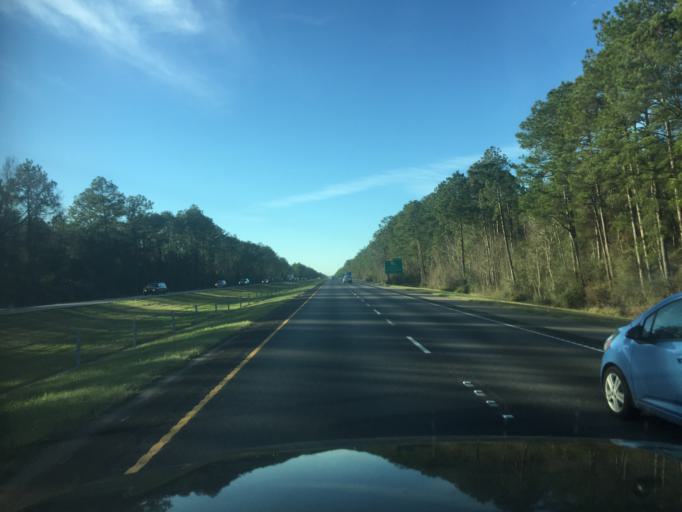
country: US
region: Louisiana
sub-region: Saint Tammany Parish
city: Lacombe
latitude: 30.3425
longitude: -89.9016
